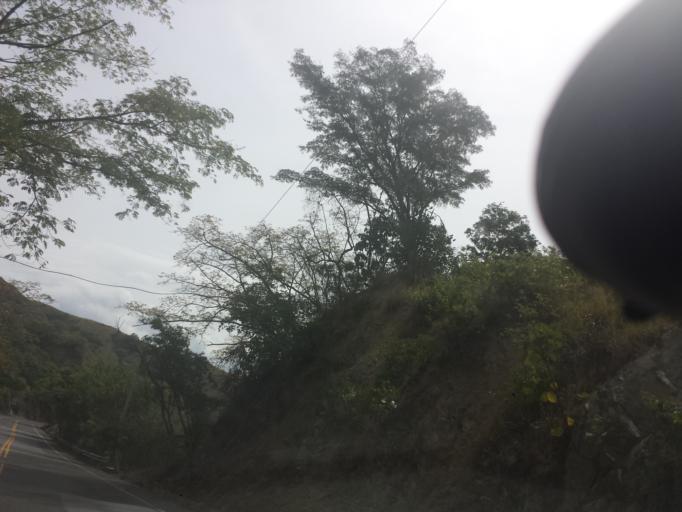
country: CO
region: Antioquia
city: Antioquia
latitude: 6.5738
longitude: -75.8387
